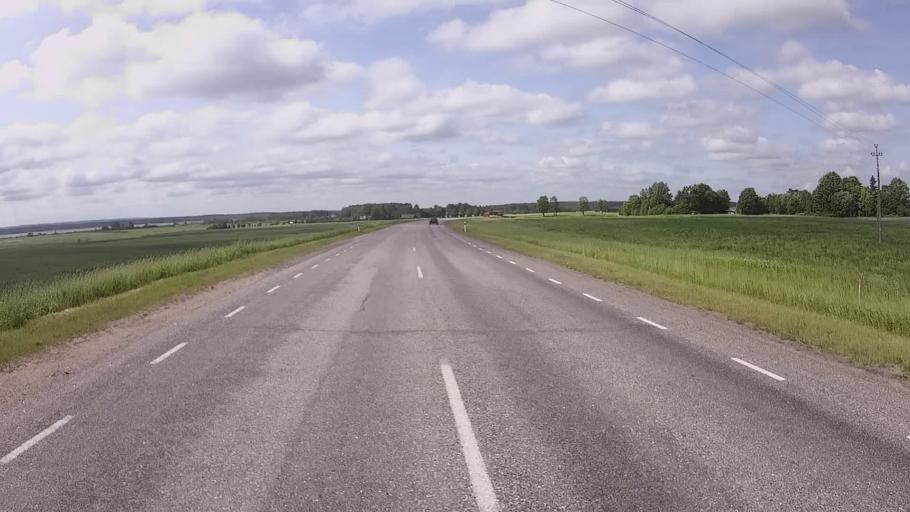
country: EE
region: Vorumaa
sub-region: Voru linn
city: Voru
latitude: 57.8672
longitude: 26.9251
